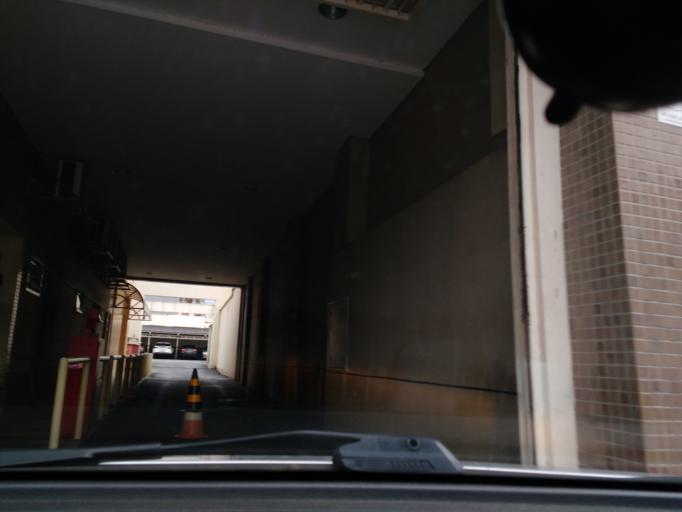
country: BR
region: Parana
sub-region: Curitiba
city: Curitiba
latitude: -25.4358
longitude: -49.2836
